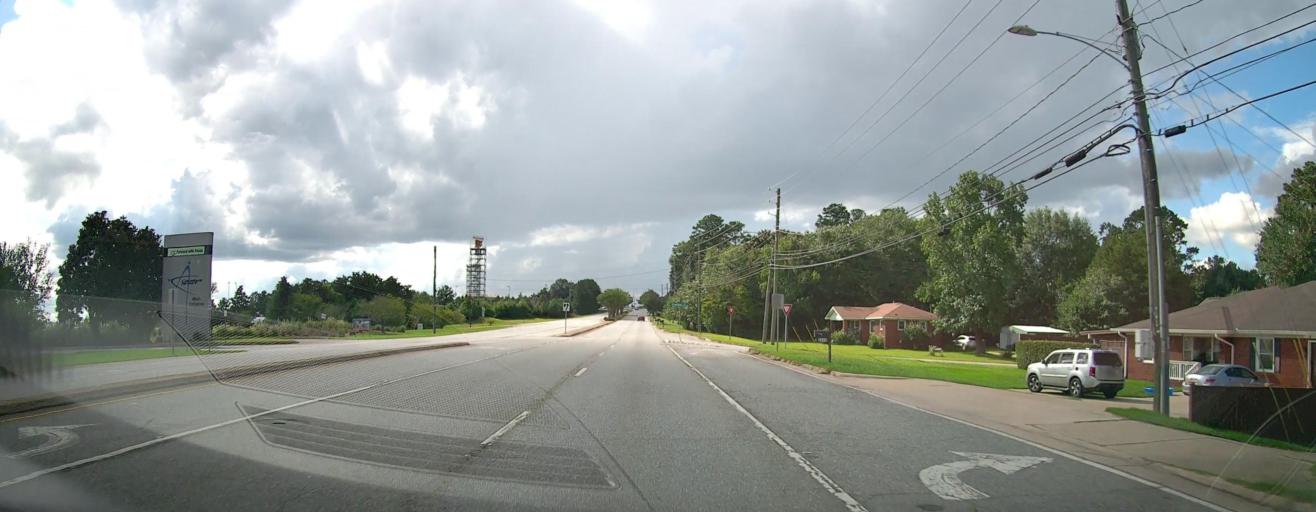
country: US
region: Georgia
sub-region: Muscogee County
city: Columbus
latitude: 32.5199
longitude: -84.9397
